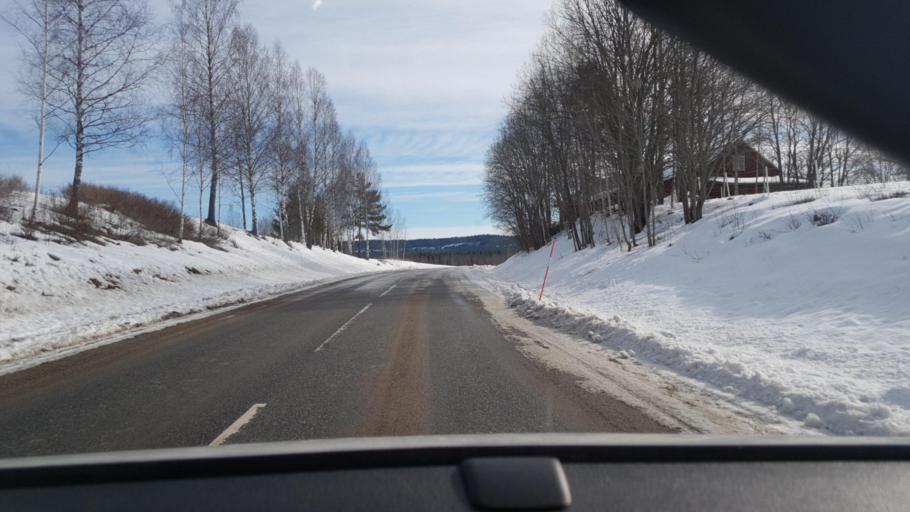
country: SE
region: Vaermland
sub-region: Eda Kommun
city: Amotfors
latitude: 59.6840
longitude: 12.1078
